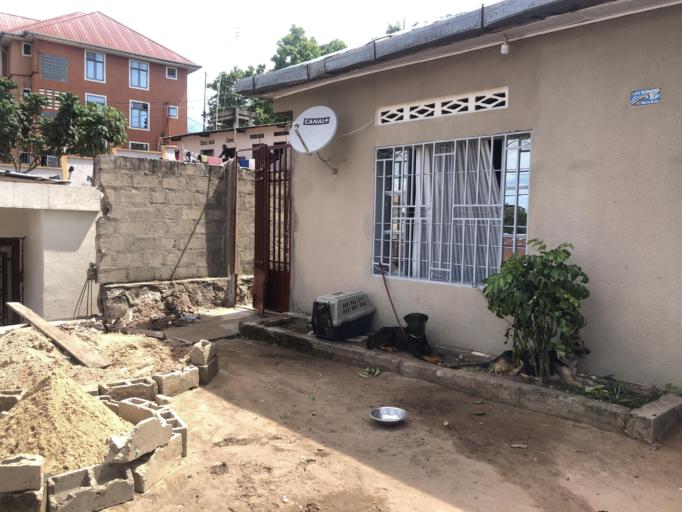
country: CD
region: Kinshasa
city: Kinshasa
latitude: -4.3467
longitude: 15.2212
